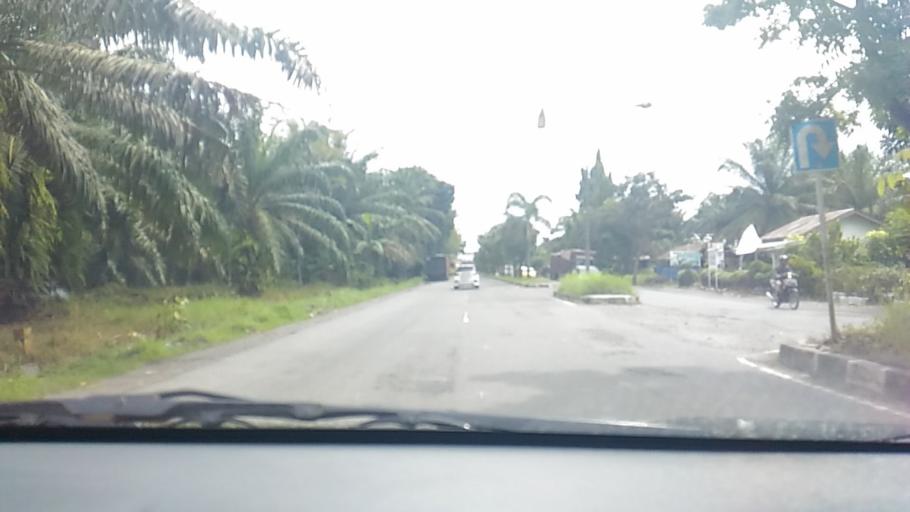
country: ID
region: North Sumatra
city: Binjai
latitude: 3.6504
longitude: 98.5130
